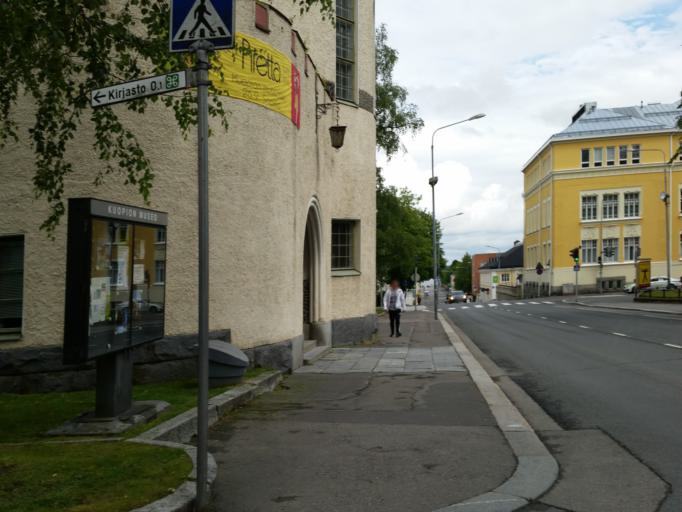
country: FI
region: Northern Savo
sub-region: Kuopio
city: Kuopio
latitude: 62.8921
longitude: 27.6864
